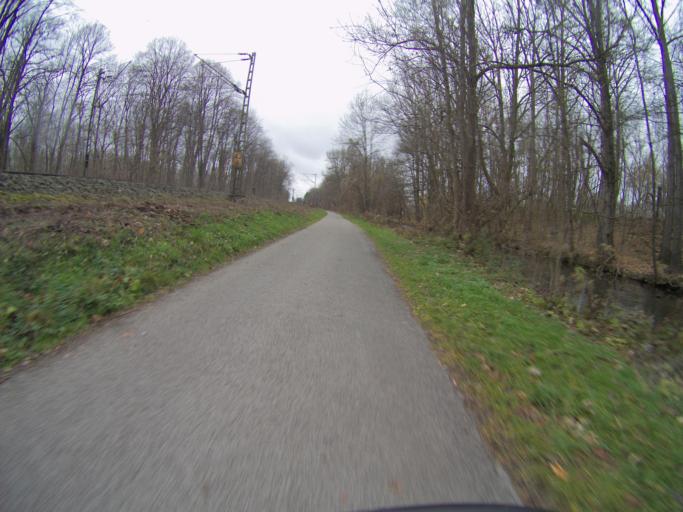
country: DE
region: Bavaria
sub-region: Upper Bavaria
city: Marzling
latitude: 48.4080
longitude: 11.7767
